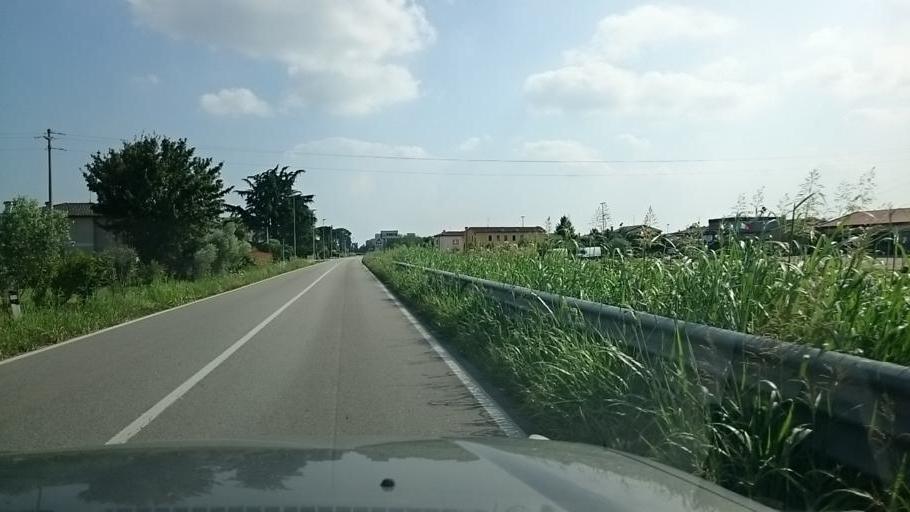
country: IT
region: Veneto
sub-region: Provincia di Padova
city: Cavino
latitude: 45.5247
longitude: 11.8684
